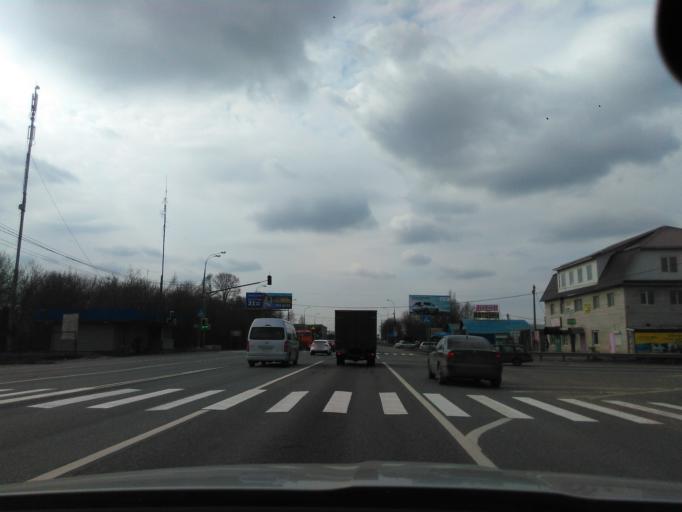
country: RU
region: Moskovskaya
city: Sheremet'yevskiy
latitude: 55.9943
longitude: 37.5340
